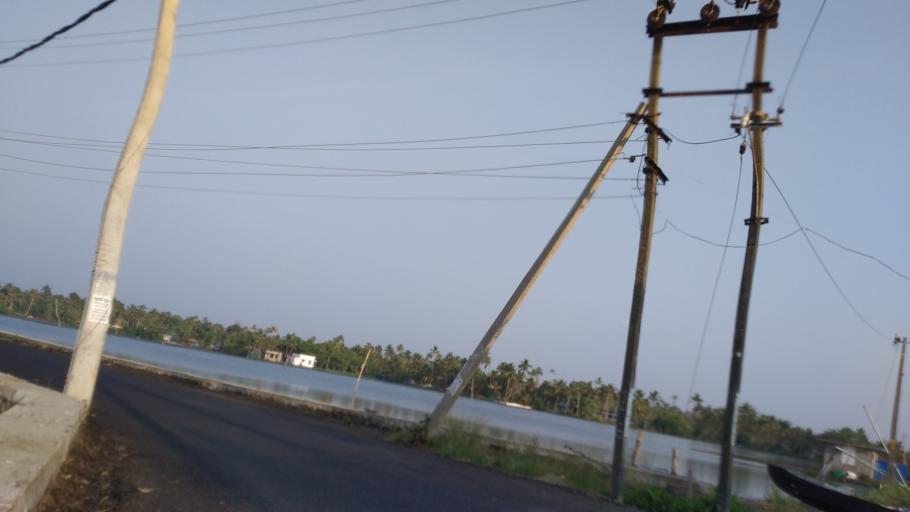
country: IN
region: Kerala
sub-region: Ernakulam
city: Elur
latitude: 10.1065
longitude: 76.1935
